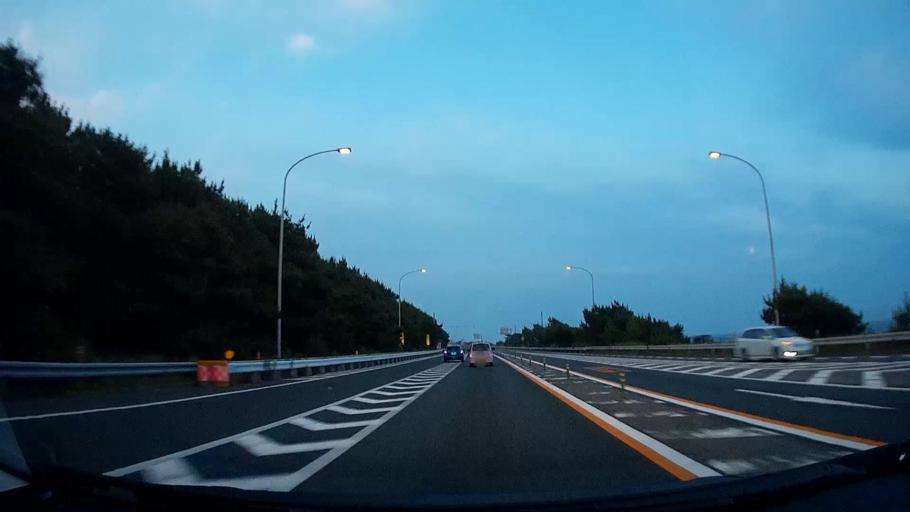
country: JP
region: Shizuoka
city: Kosai-shi
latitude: 34.6794
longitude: 137.5361
